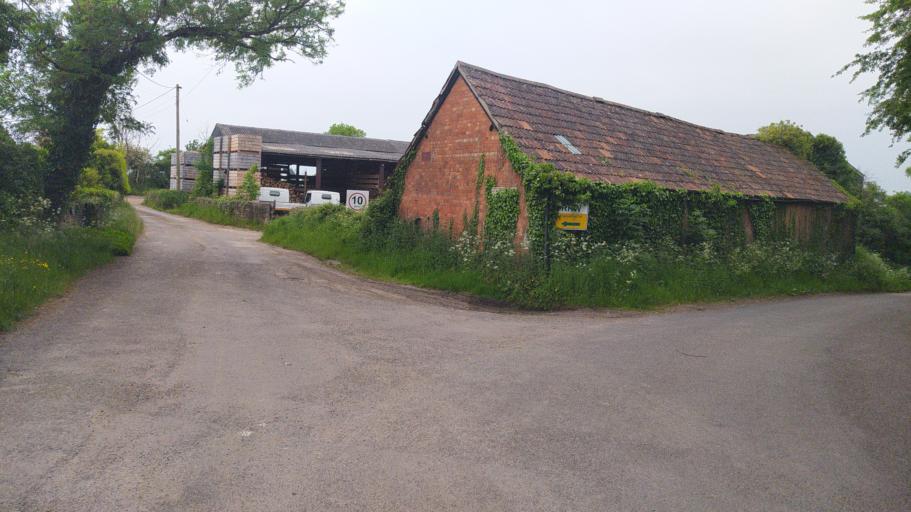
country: GB
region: England
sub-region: Wiltshire
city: Seend
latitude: 51.3490
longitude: -2.0717
